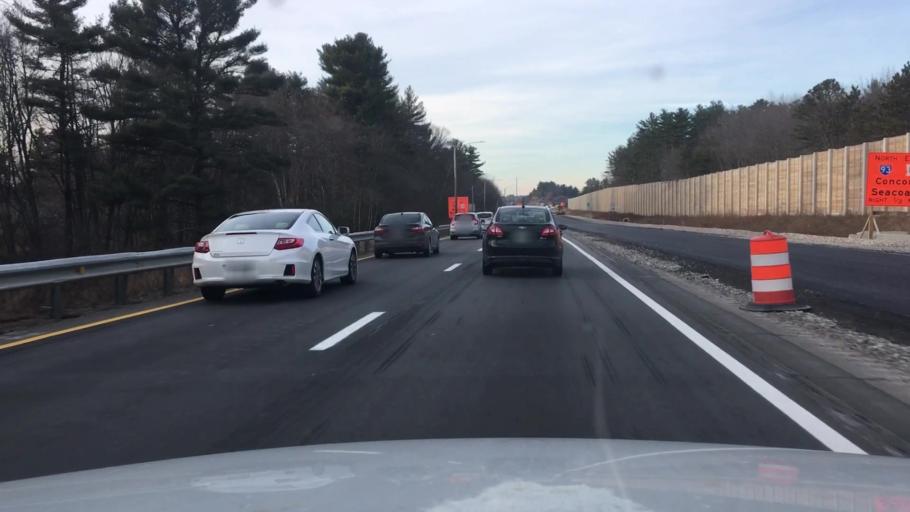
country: US
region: New Hampshire
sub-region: Rockingham County
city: Auburn
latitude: 42.9489
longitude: -71.3957
